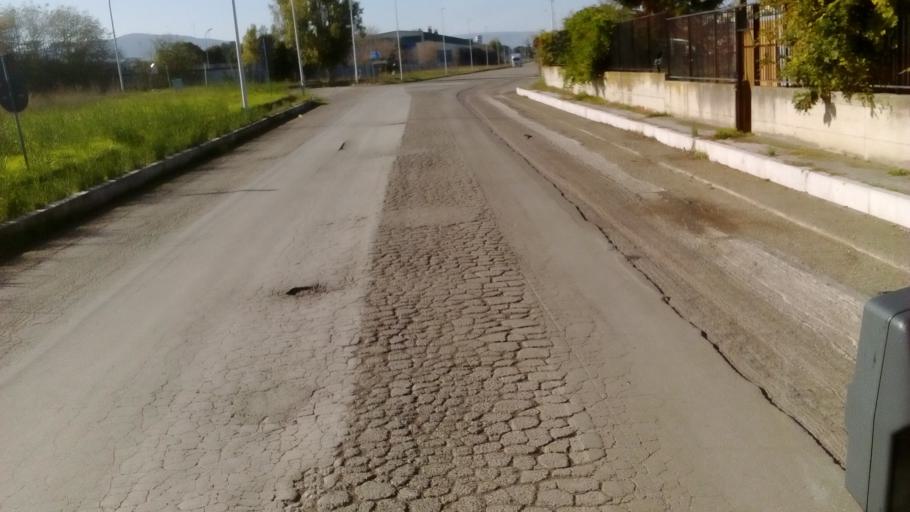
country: IT
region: Basilicate
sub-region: Provincia di Potenza
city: Melfi
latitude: 41.0758
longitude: 15.6865
